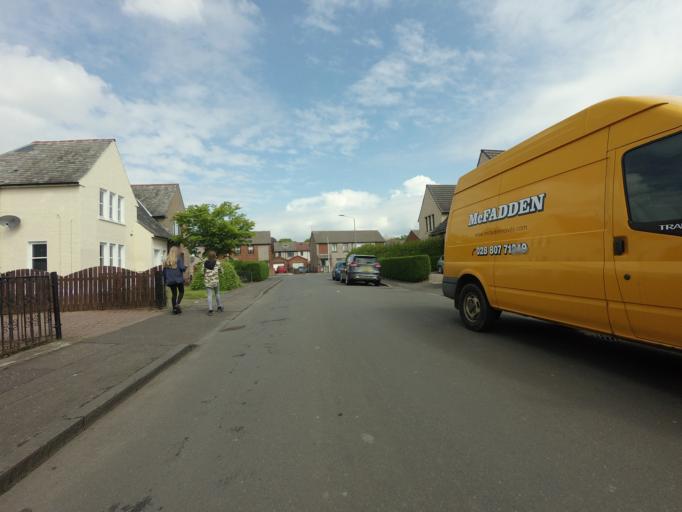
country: GB
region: Scotland
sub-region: Falkirk
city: Falkirk
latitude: 56.0032
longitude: -3.7644
